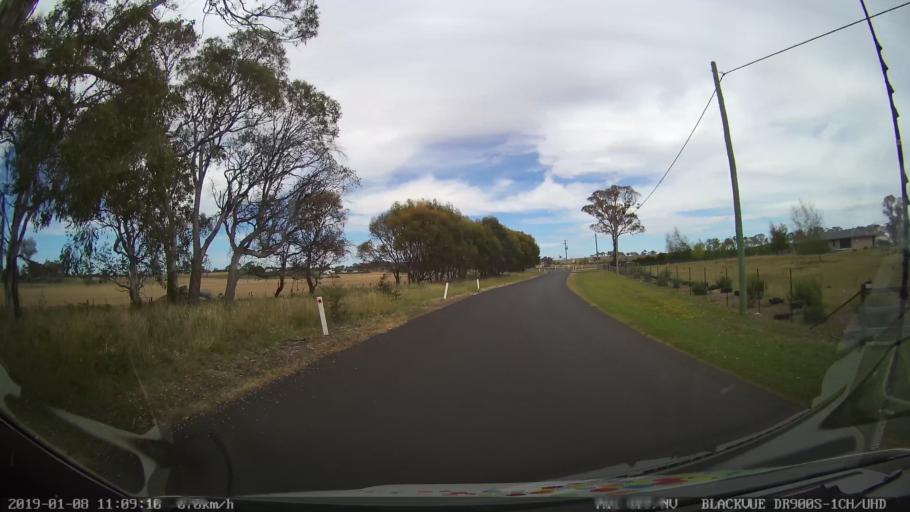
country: AU
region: New South Wales
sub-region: Guyra
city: Guyra
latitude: -30.2247
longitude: 151.6505
